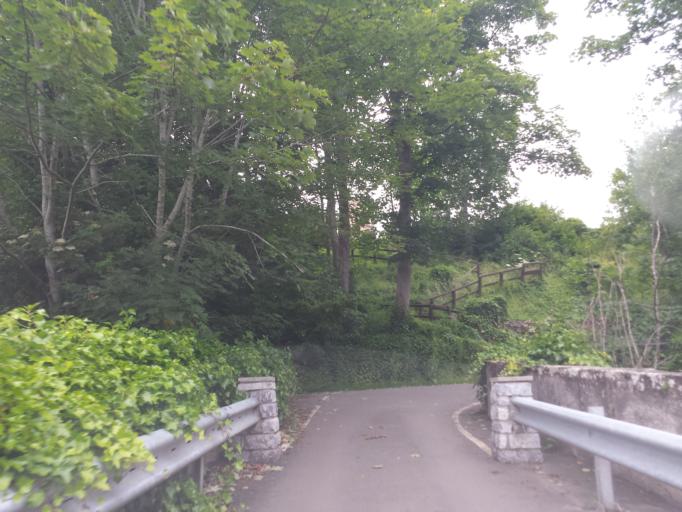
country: GB
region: Scotland
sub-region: Highland
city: Nairn
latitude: 57.5069
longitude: -4.0044
